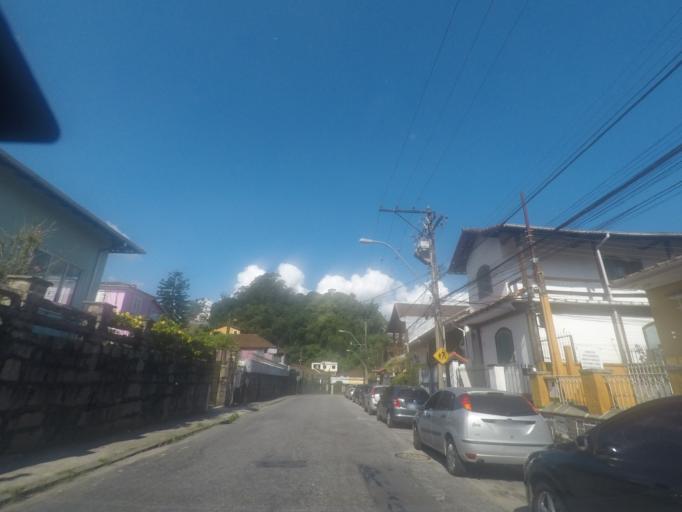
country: BR
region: Rio de Janeiro
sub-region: Petropolis
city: Petropolis
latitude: -22.5189
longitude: -43.1923
